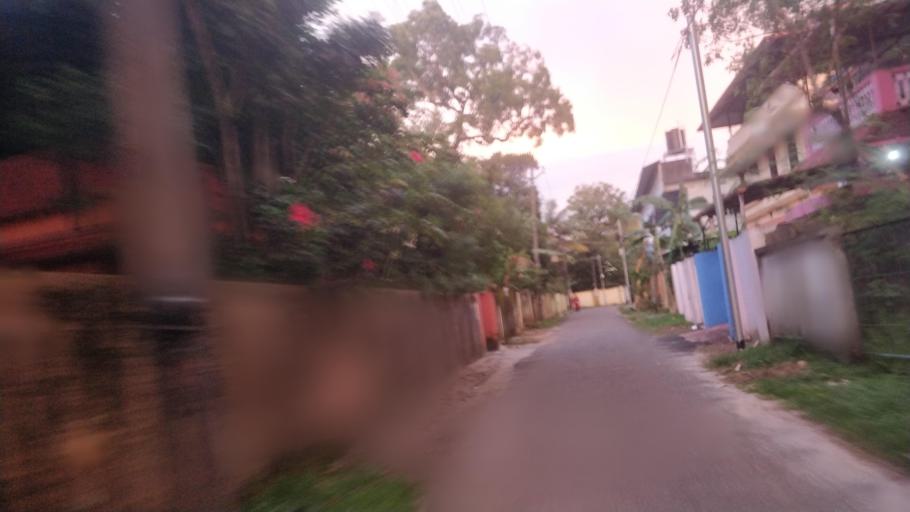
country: IN
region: Kerala
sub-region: Alappuzha
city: Shertallai
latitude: 9.6739
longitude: 76.3384
